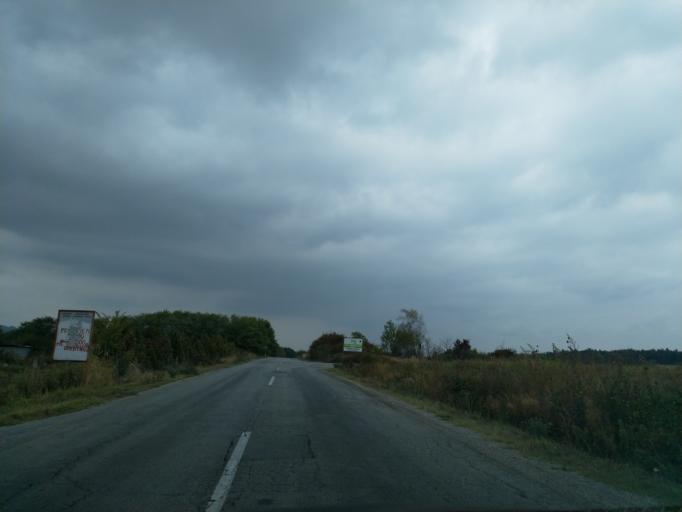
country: RS
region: Central Serbia
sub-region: Pomoravski Okrug
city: Jagodina
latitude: 44.0180
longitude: 21.1977
